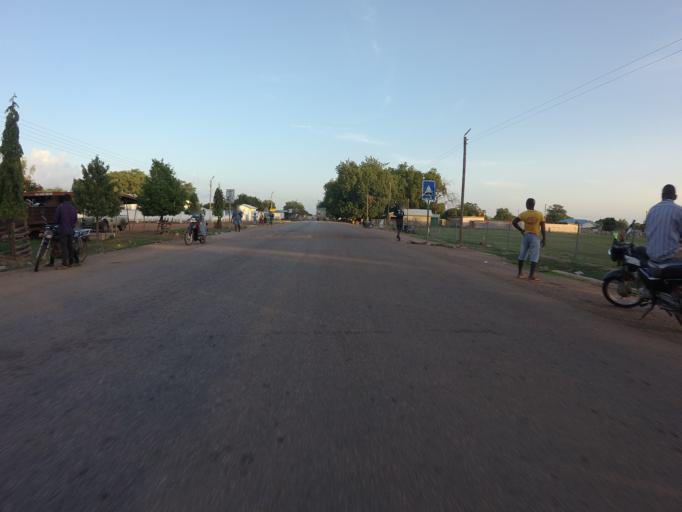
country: GH
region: Upper East
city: Navrongo
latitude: 10.9692
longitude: -1.1022
